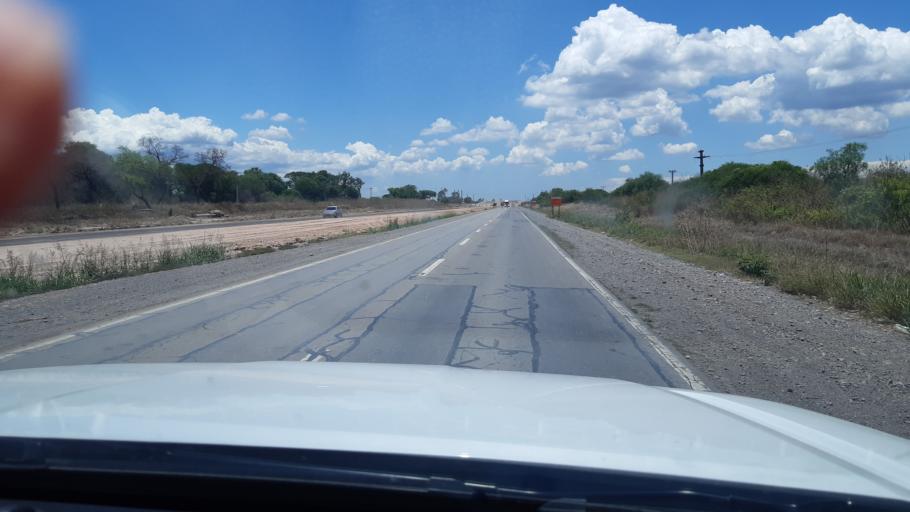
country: AR
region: Salta
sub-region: Departamento de General Guemes
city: General Martin Miguel de Guemes
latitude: -24.4928
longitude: -65.0476
